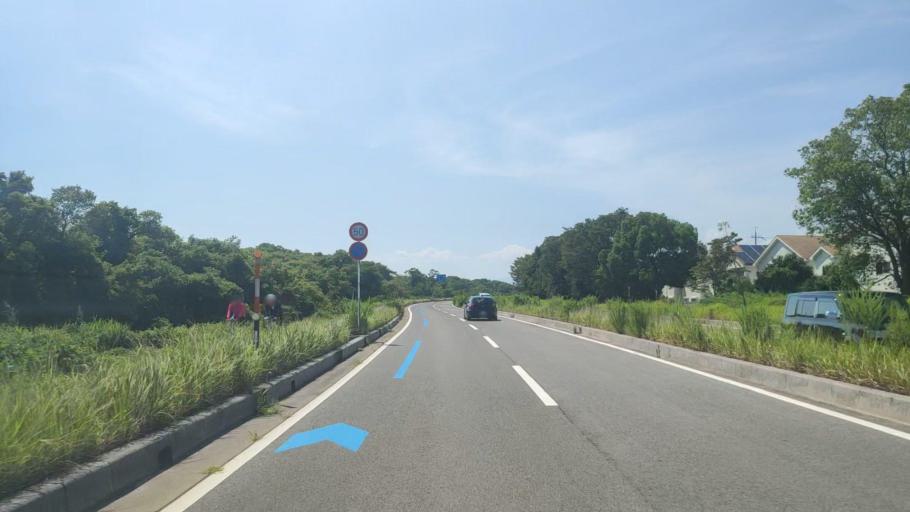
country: JP
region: Shiga Prefecture
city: Nagahama
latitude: 35.3837
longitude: 136.2516
